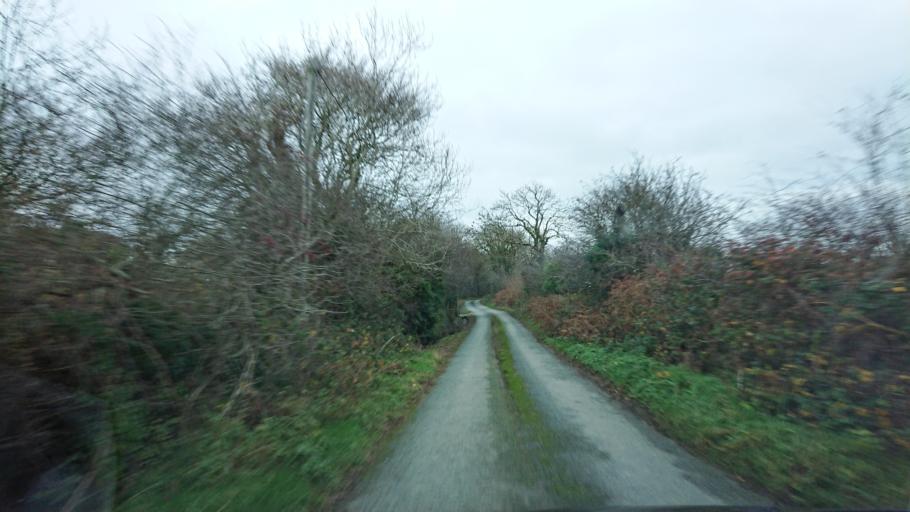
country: IE
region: Munster
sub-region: Waterford
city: Dunmore East
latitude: 52.1931
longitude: -7.0367
